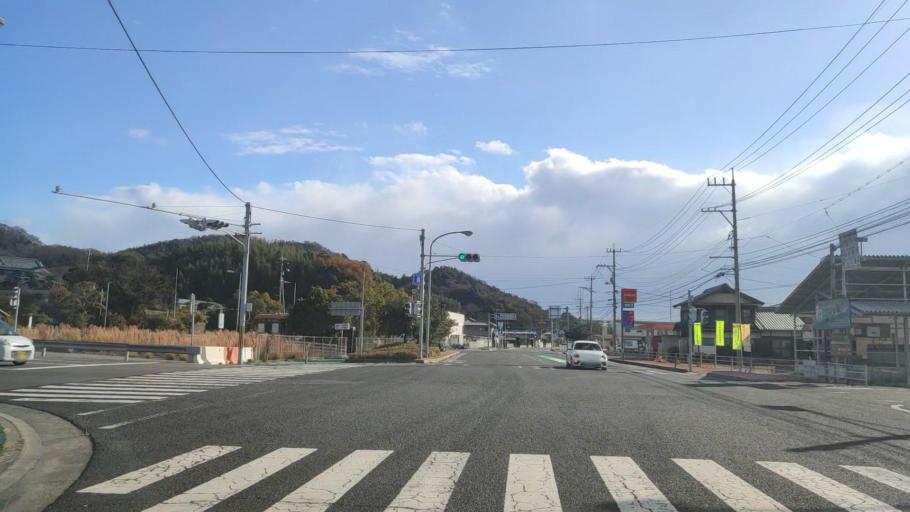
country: JP
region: Hiroshima
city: Innoshima
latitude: 34.2052
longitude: 133.0751
